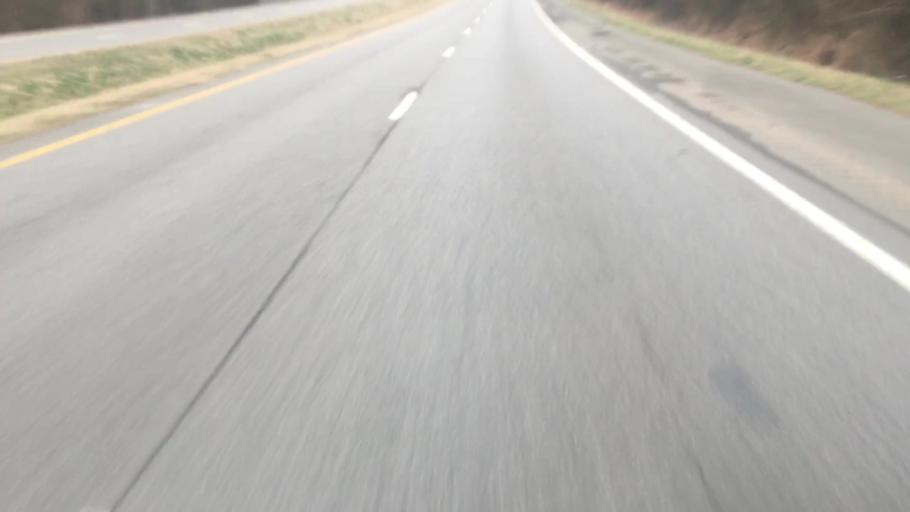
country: US
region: Alabama
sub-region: Jefferson County
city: Graysville
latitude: 33.6841
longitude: -86.9747
